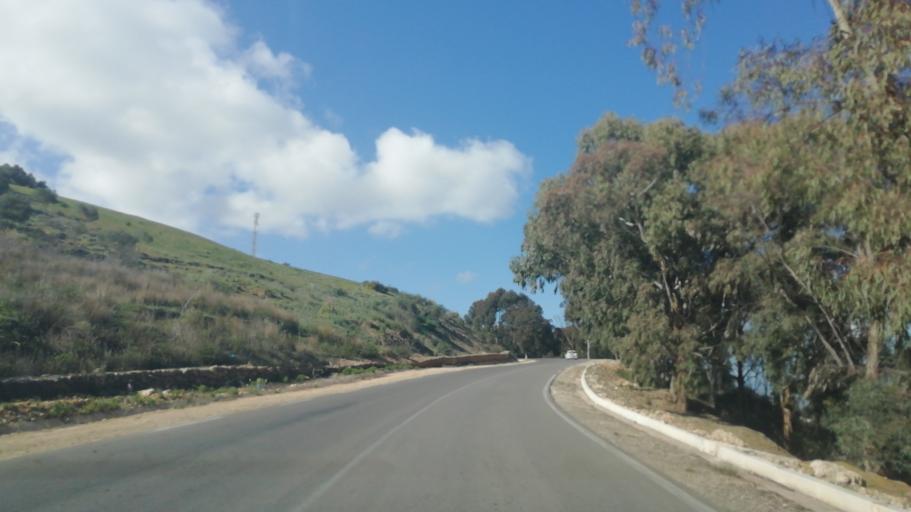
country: DZ
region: Relizane
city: Relizane
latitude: 36.0857
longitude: 0.4746
